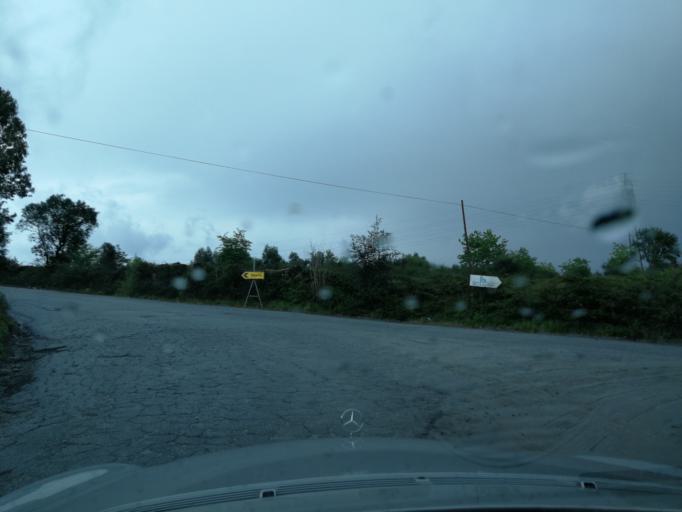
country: PT
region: Braga
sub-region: Vila Nova de Famalicao
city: Joane
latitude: 41.4614
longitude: -8.4324
